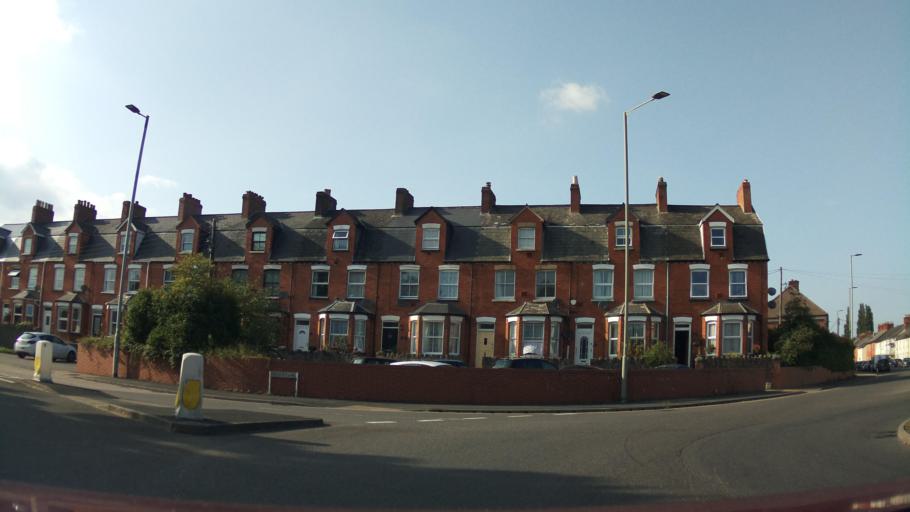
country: GB
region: England
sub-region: Devon
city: Tiverton
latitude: 50.8998
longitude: -3.4912
